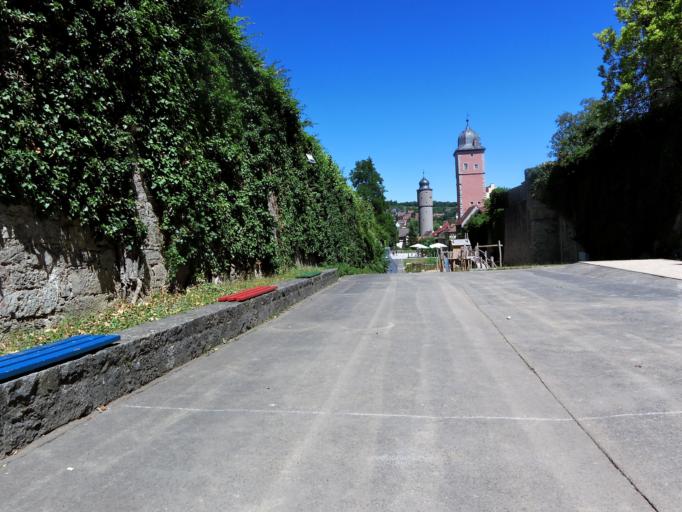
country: DE
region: Bavaria
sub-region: Regierungsbezirk Unterfranken
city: Ochsenfurt
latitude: 49.6638
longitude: 10.0613
